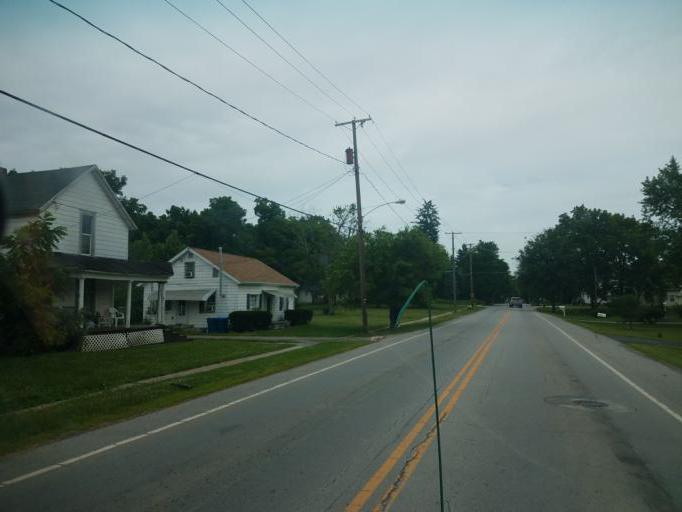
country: US
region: Ohio
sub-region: Hardin County
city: Ada
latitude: 40.7609
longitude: -83.8232
